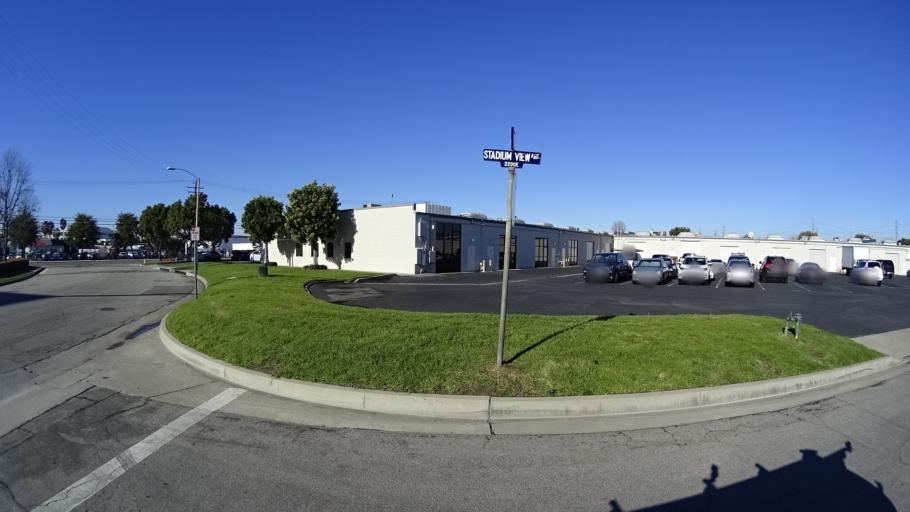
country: US
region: California
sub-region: Orange County
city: Orange
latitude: 33.8070
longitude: -117.8838
